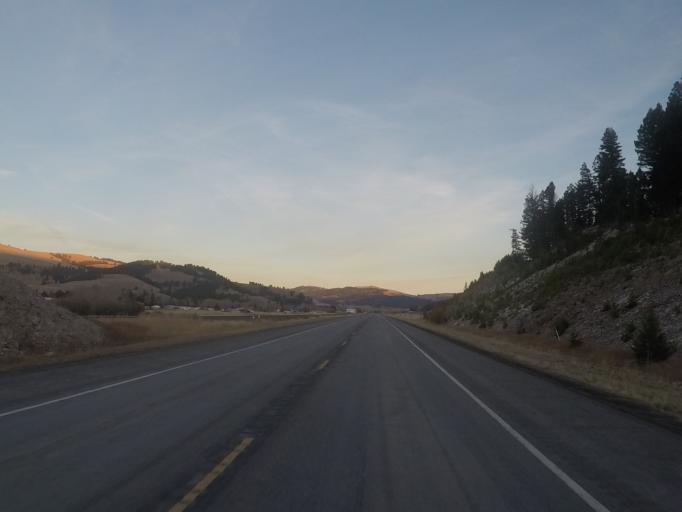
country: US
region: Montana
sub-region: Powell County
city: Deer Lodge
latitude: 46.5651
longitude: -112.4478
